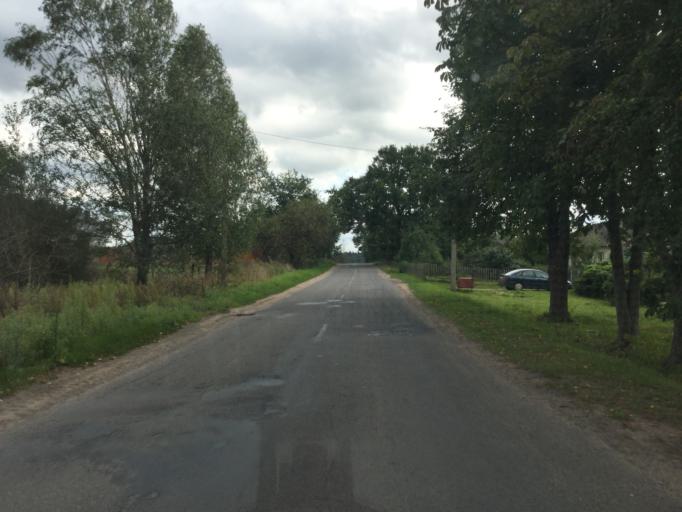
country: BY
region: Vitebsk
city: Vitebsk
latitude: 55.1446
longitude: 30.2848
